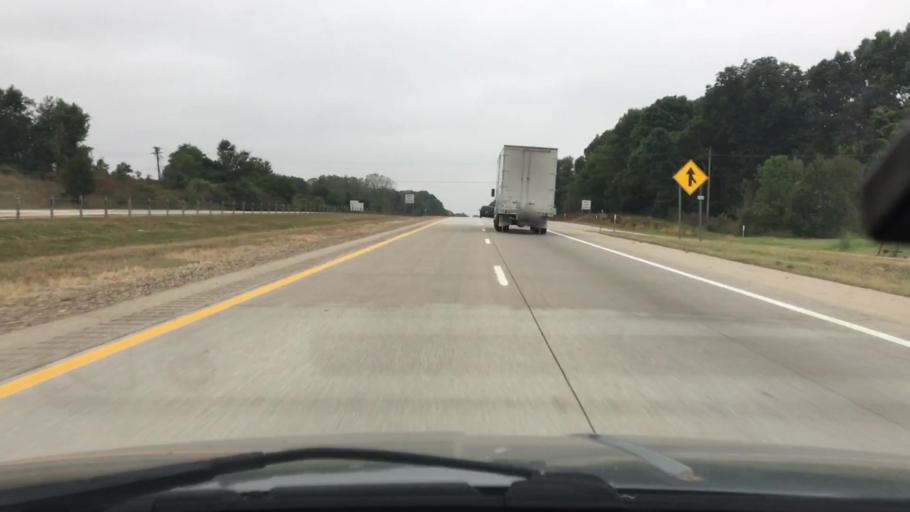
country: US
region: Michigan
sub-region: Van Buren County
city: Paw Paw
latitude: 42.1985
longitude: -85.9694
